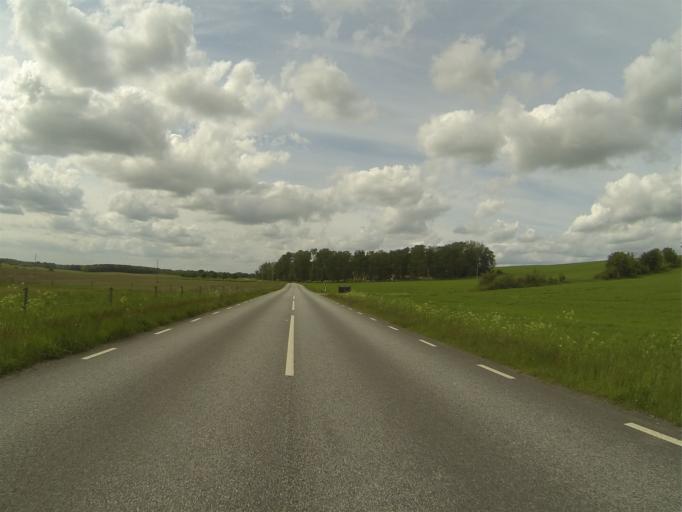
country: SE
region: Skane
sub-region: Sjobo Kommun
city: Sjoebo
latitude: 55.6751
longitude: 13.6592
